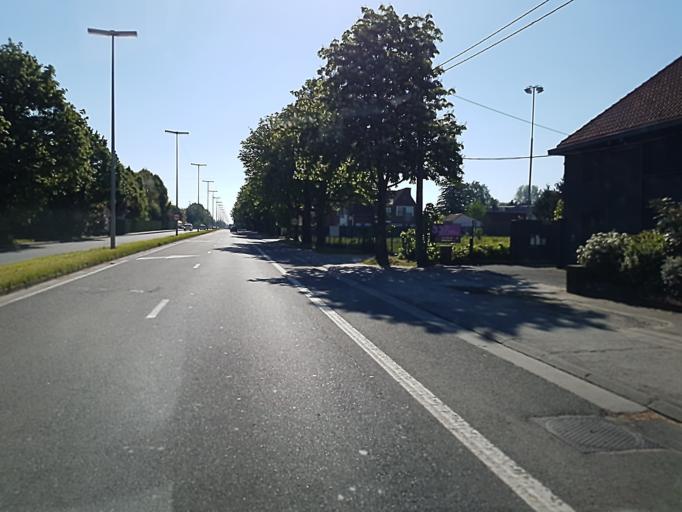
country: BE
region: Wallonia
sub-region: Province du Hainaut
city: Mouscron
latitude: 50.7426
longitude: 3.2414
